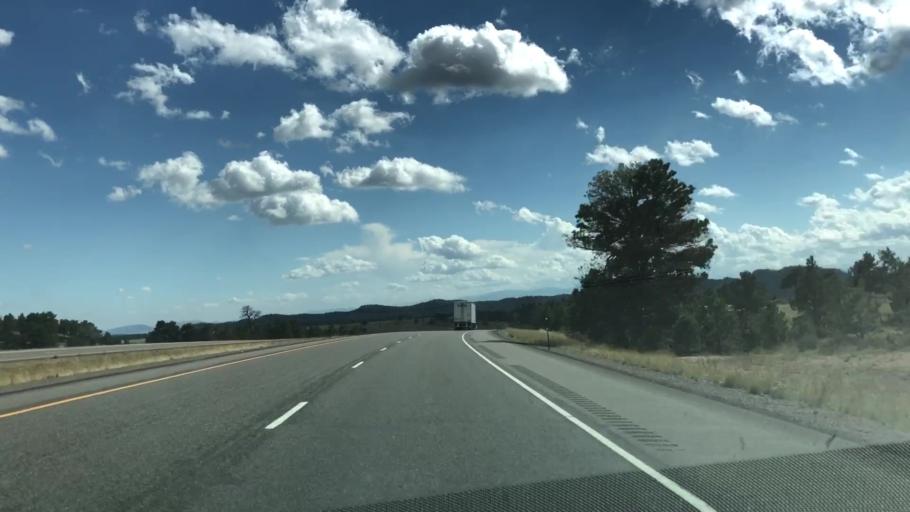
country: US
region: Wyoming
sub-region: Albany County
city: Laramie
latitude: 41.0130
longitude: -105.4200
